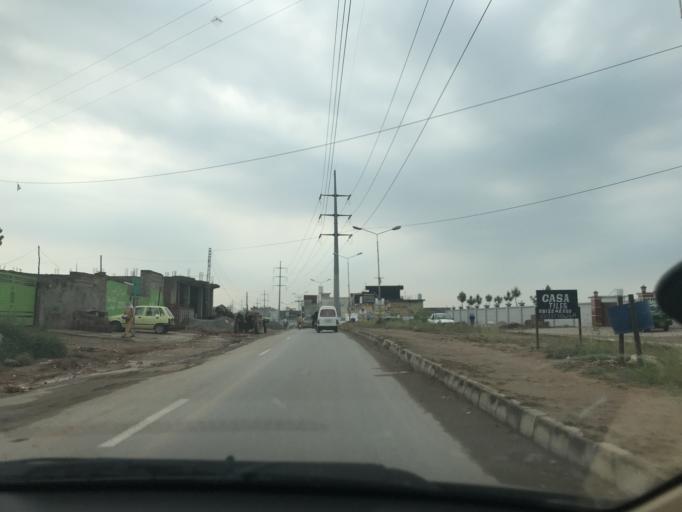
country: PK
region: Islamabad
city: Islamabad
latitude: 33.6850
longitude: 73.1618
